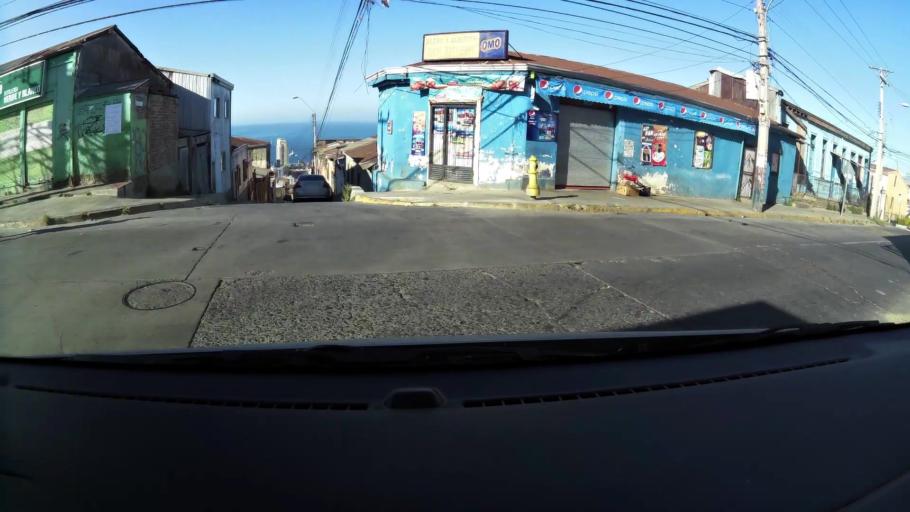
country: CL
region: Valparaiso
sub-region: Provincia de Valparaiso
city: Valparaiso
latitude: -33.0528
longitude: -71.6181
